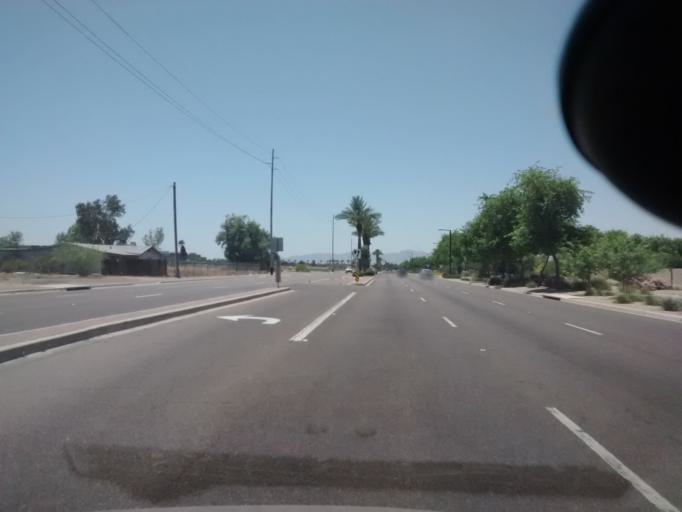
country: US
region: Arizona
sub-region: Maricopa County
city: Peoria
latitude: 33.5377
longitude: -112.2485
